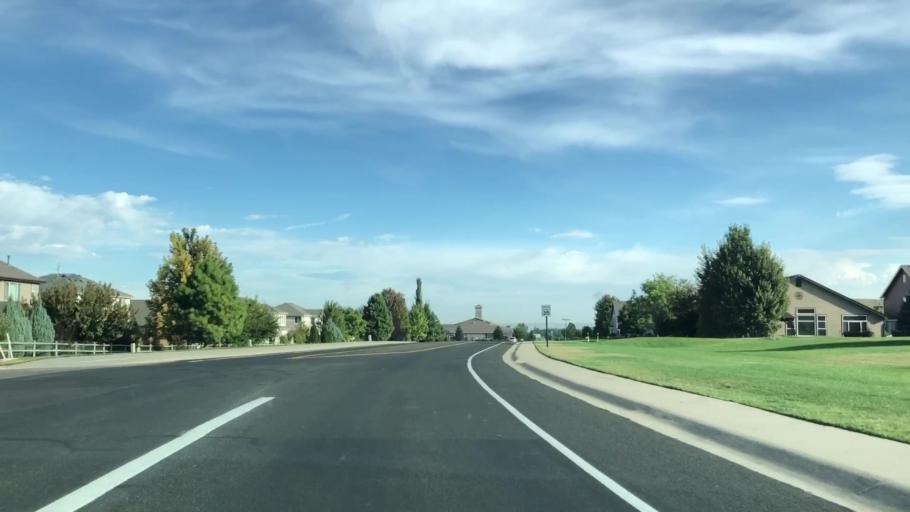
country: US
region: Colorado
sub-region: Weld County
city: Windsor
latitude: 40.4705
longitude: -104.9794
